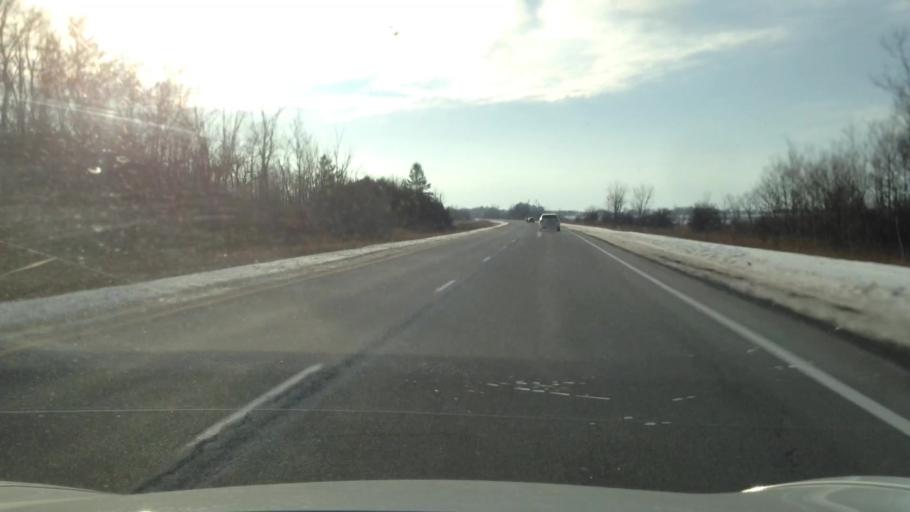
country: CA
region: Ontario
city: Casselman
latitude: 45.3677
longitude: -74.8639
